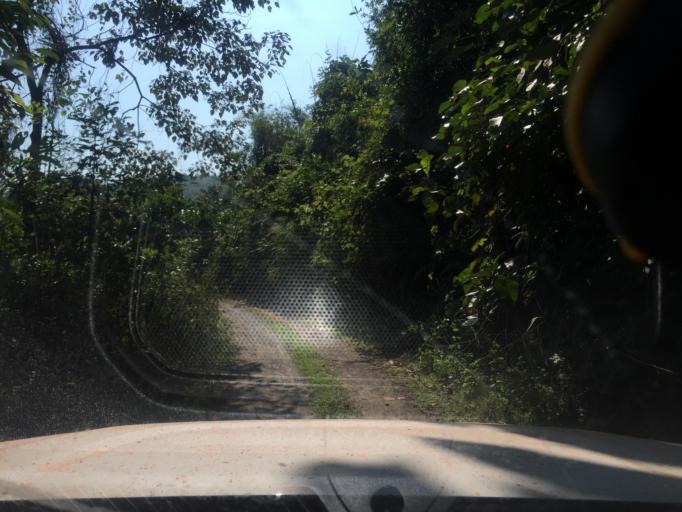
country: LA
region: Phongsali
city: Phongsali
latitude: 21.6884
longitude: 102.4093
